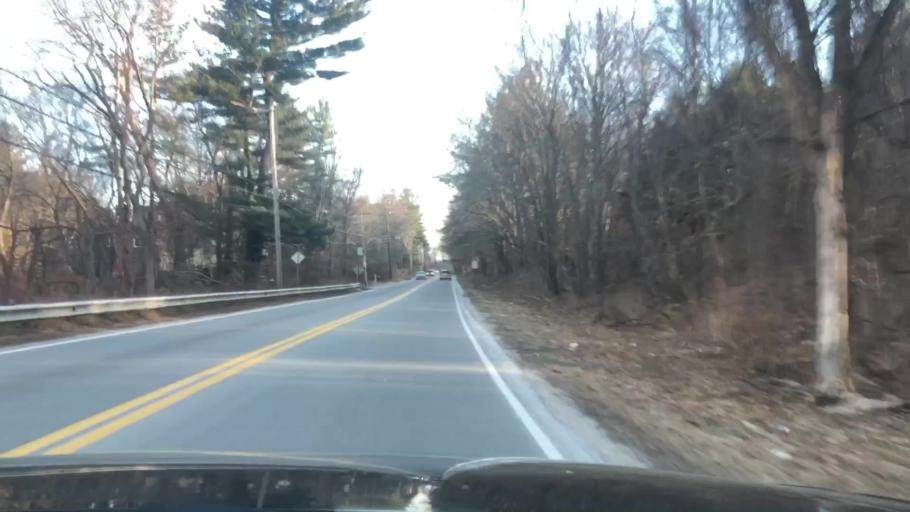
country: US
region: Massachusetts
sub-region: Worcester County
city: Bolton
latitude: 42.4452
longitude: -71.6246
